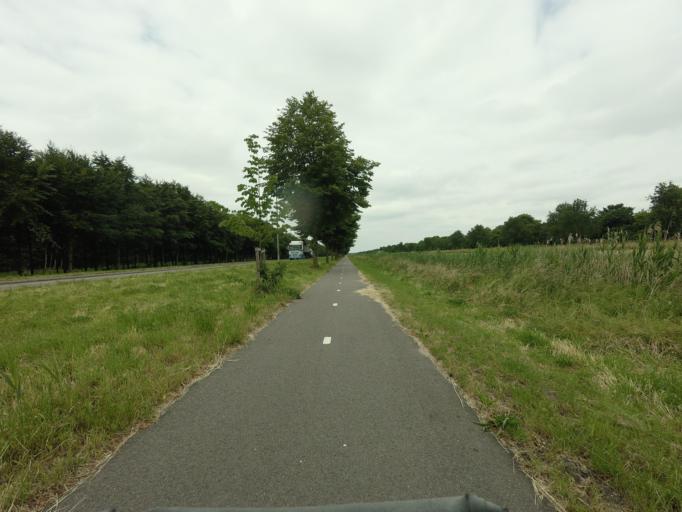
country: NL
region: Flevoland
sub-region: Gemeente Zeewolde
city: Zeewolde
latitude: 52.3287
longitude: 5.5151
